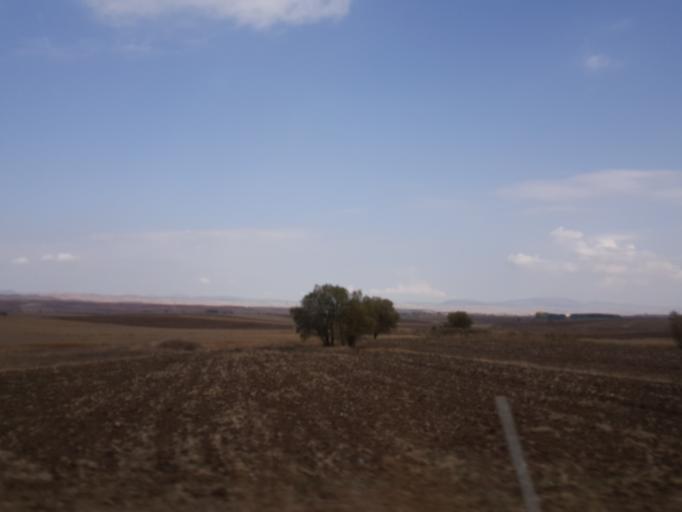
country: TR
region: Corum
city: Alaca
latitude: 40.1397
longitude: 34.7797
